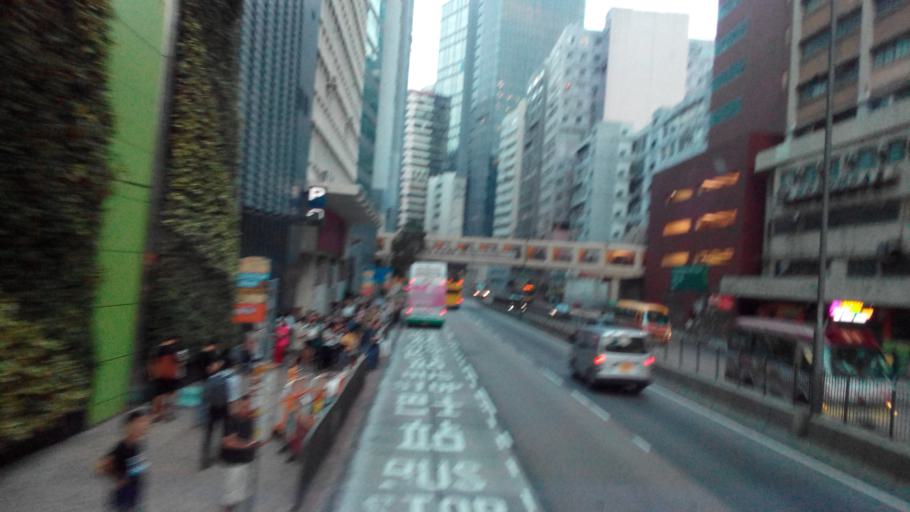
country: HK
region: Wanchai
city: Wan Chai
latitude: 22.2486
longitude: 114.1632
